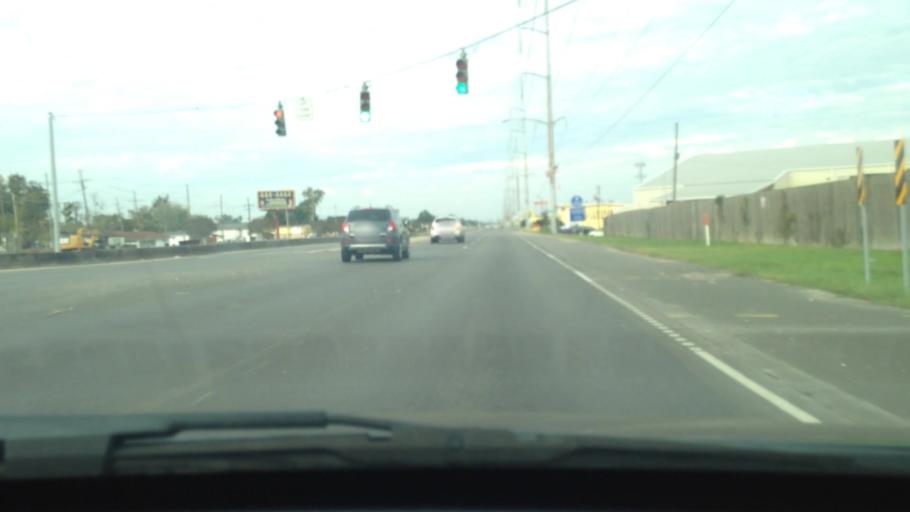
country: US
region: Louisiana
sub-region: Jefferson Parish
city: River Ridge
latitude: 29.9780
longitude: -90.2129
